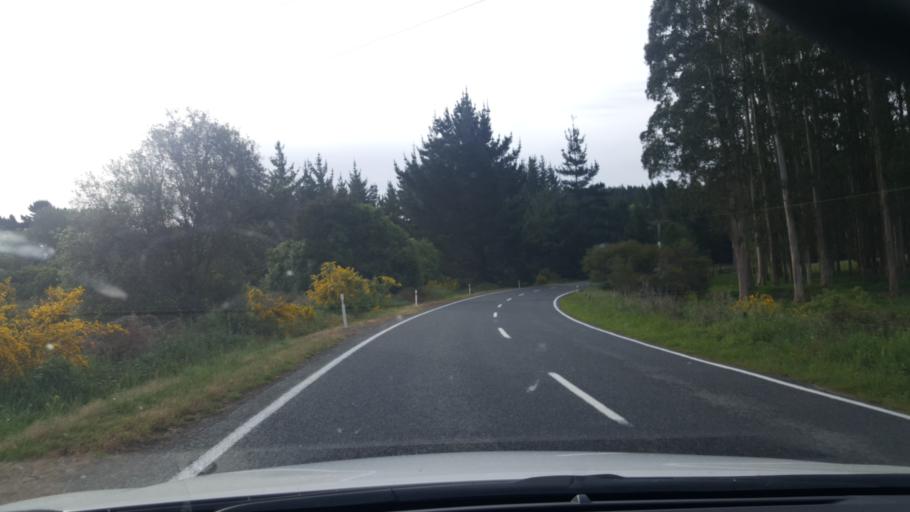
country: NZ
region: Waikato
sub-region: Taupo District
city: Taupo
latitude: -38.6137
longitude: 176.1225
